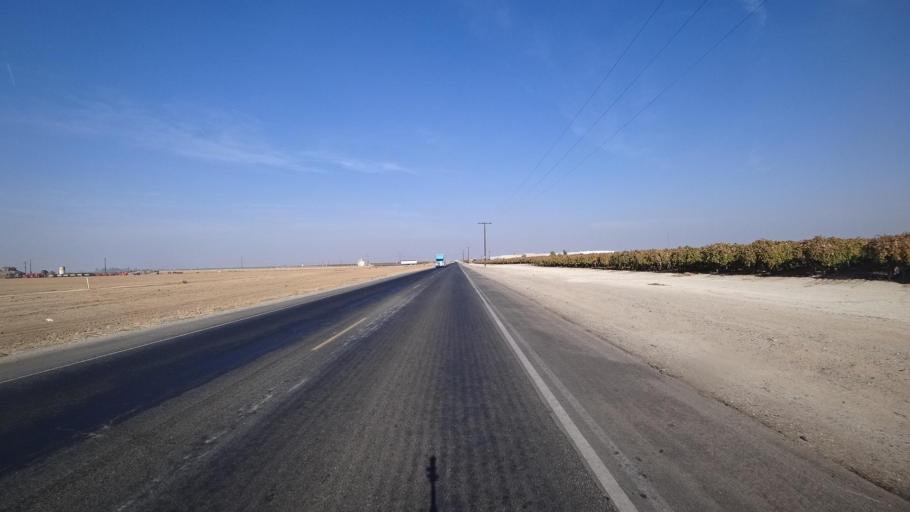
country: US
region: California
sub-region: Kern County
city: McFarland
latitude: 35.7152
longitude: -119.1615
